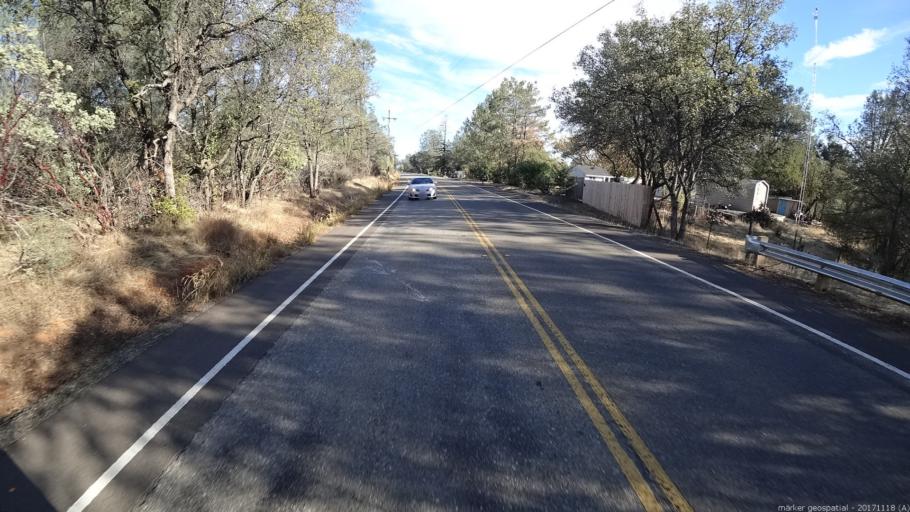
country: US
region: California
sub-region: Shasta County
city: Redding
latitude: 40.4781
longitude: -122.4239
